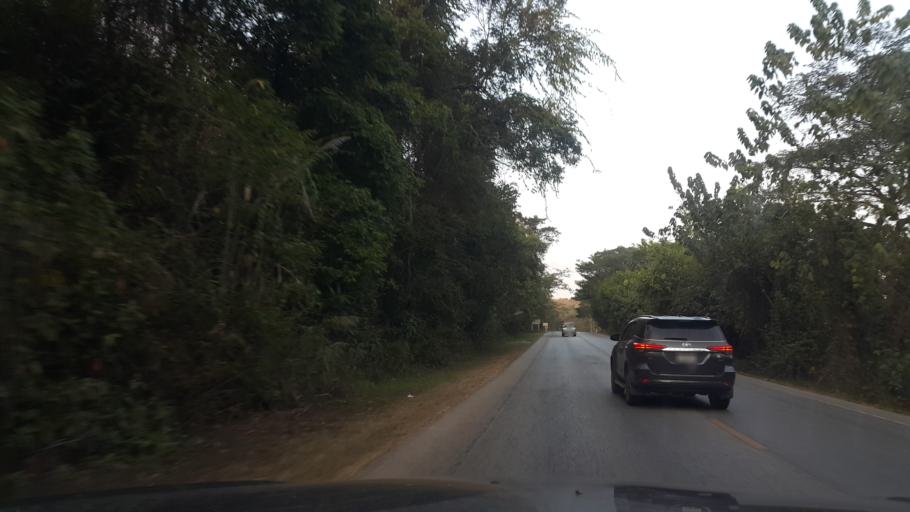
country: TH
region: Loei
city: Loei
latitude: 17.4686
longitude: 101.5958
